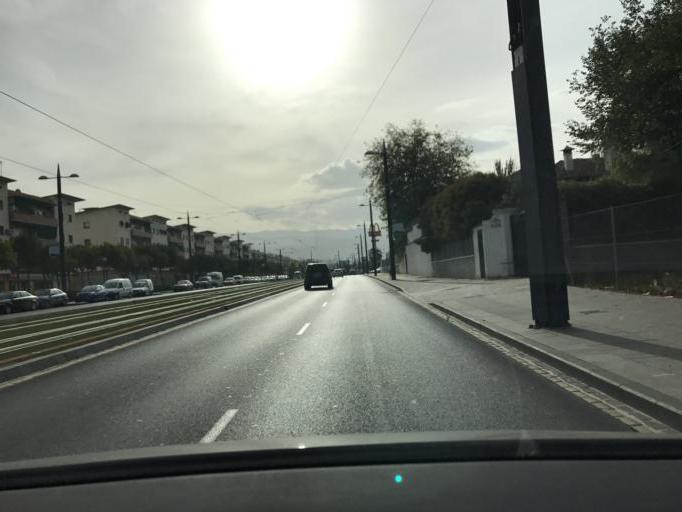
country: ES
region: Andalusia
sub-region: Provincia de Granada
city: Granada
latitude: 37.2031
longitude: -3.6164
